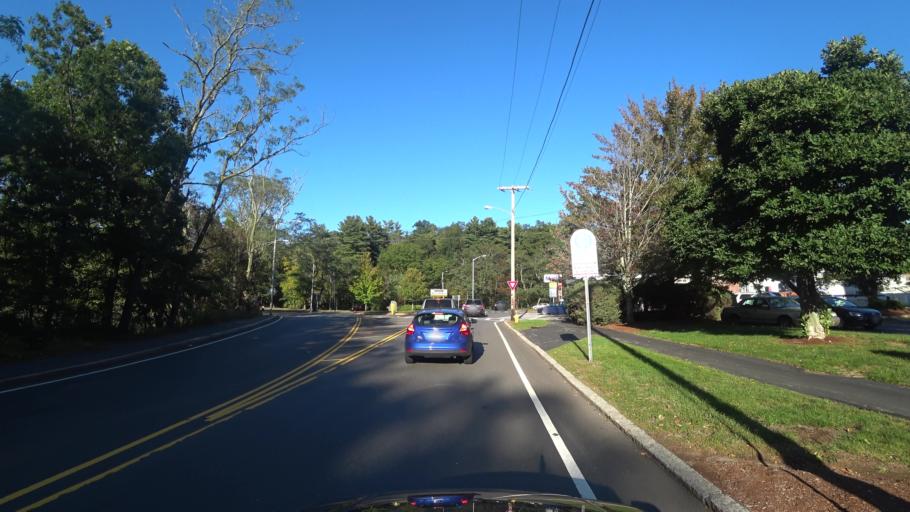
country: US
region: Massachusetts
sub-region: Middlesex County
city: Medford
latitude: 42.4420
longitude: -71.0946
